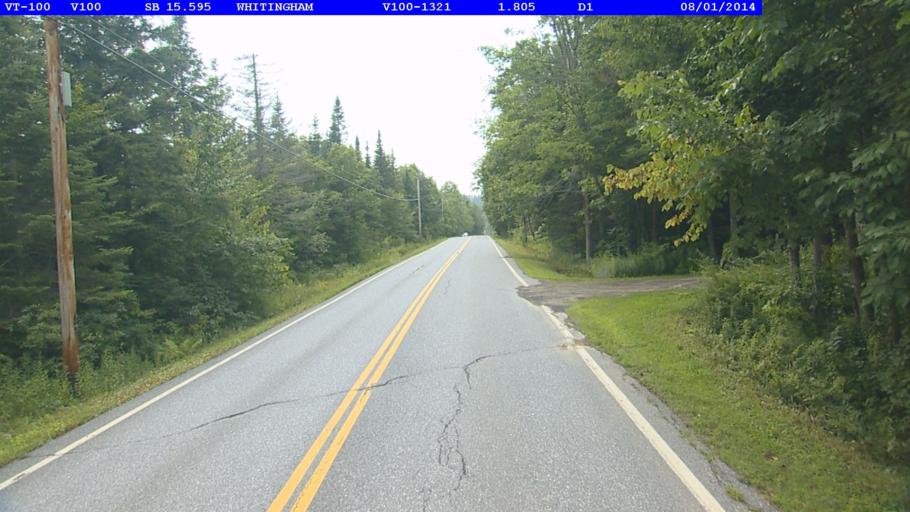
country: US
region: Massachusetts
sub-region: Franklin County
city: Charlemont
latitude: 42.7655
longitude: -72.8977
